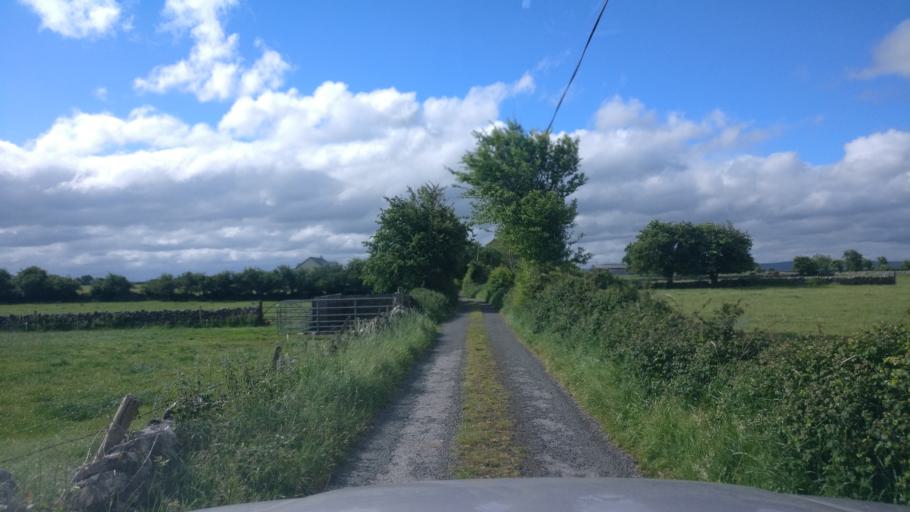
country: IE
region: Connaught
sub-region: County Galway
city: Loughrea
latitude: 53.2354
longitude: -8.6008
